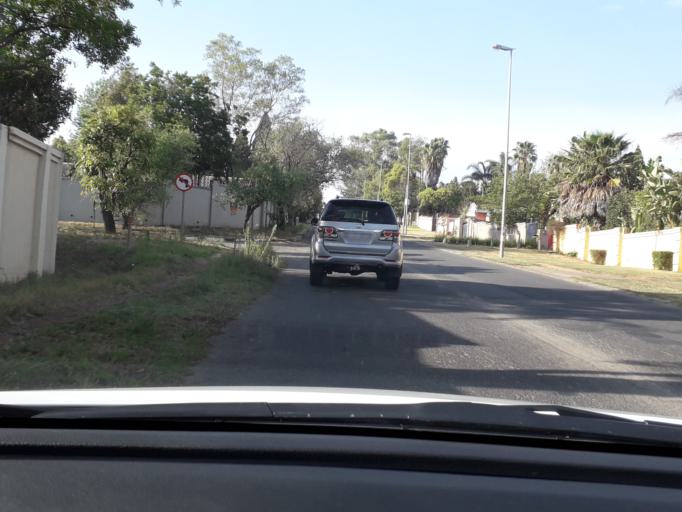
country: ZA
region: Gauteng
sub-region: West Rand District Municipality
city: Muldersdriseloop
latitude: -26.0747
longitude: 27.9455
